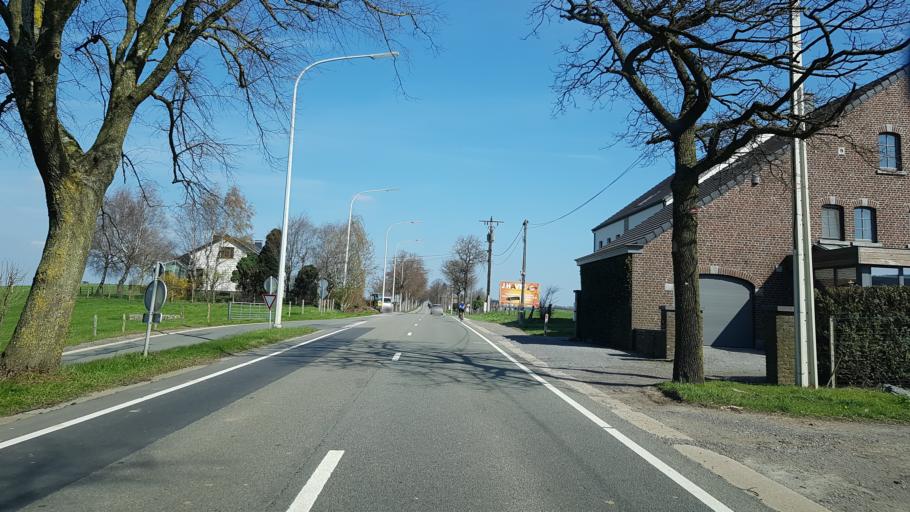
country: BE
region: Wallonia
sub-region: Province de Liege
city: Aubel
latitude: 50.6593
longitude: 5.8918
